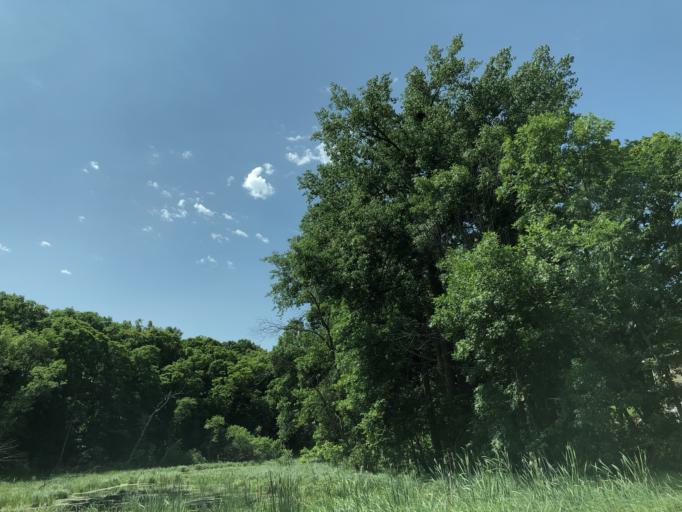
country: US
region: Minnesota
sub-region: Douglas County
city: Alexandria
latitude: 45.9351
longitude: -95.3830
